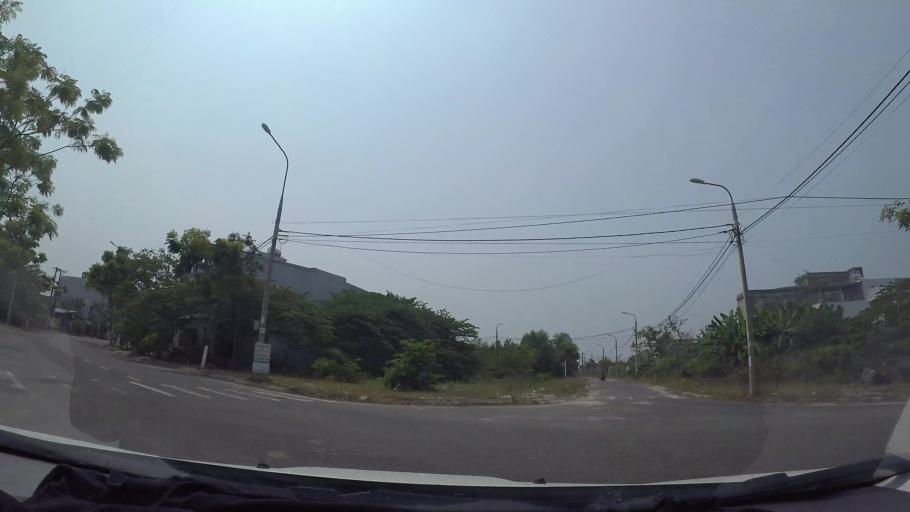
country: VN
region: Da Nang
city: Cam Le
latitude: 16.0008
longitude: 108.2040
